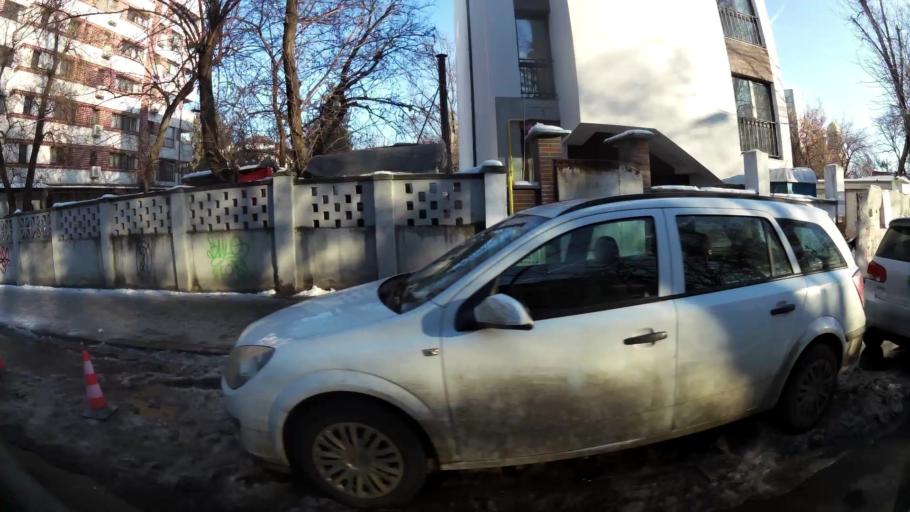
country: RO
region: Bucuresti
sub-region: Municipiul Bucuresti
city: Bucuresti
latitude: 44.4303
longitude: 26.0788
